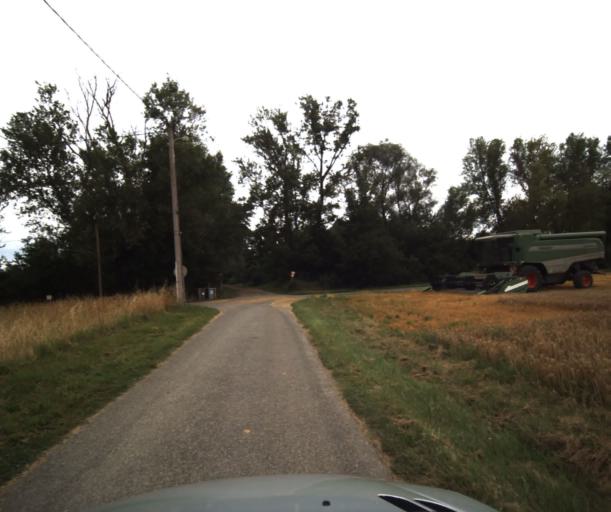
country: FR
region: Midi-Pyrenees
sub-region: Departement de la Haute-Garonne
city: Lacroix-Falgarde
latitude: 43.4757
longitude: 1.4127
